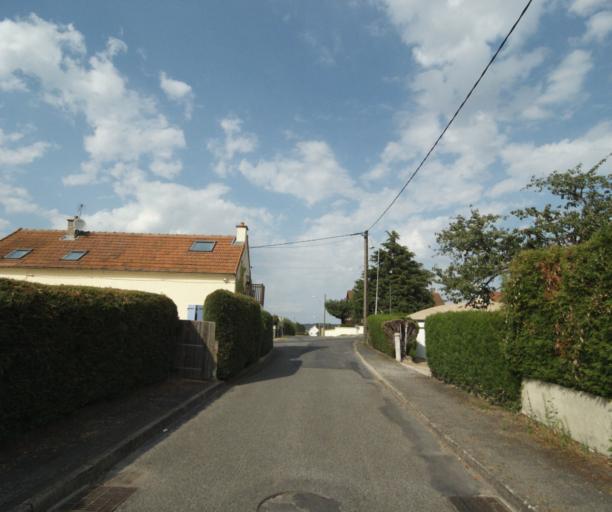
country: FR
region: Bourgogne
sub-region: Departement de Saone-et-Loire
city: Gueugnon
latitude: 46.6047
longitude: 4.0777
